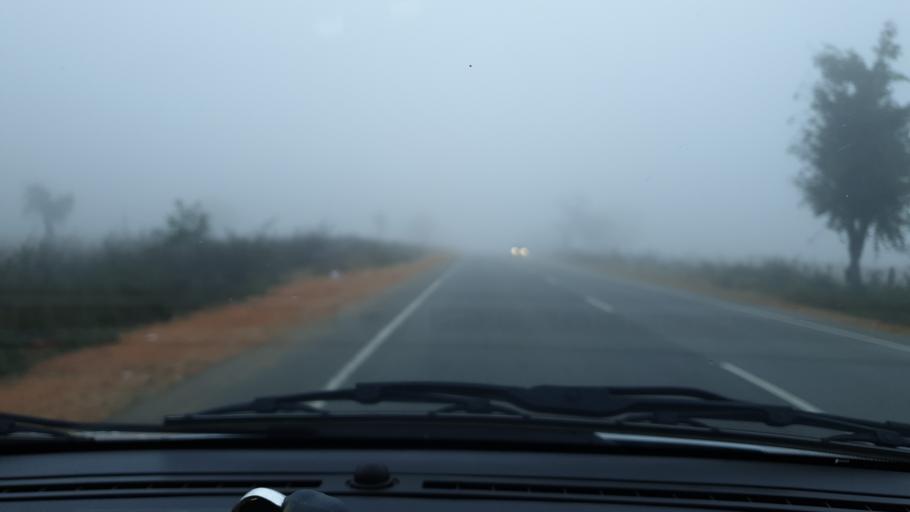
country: IN
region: Telangana
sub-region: Mahbubnagar
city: Nagar Karnul
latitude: 16.6933
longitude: 78.5190
